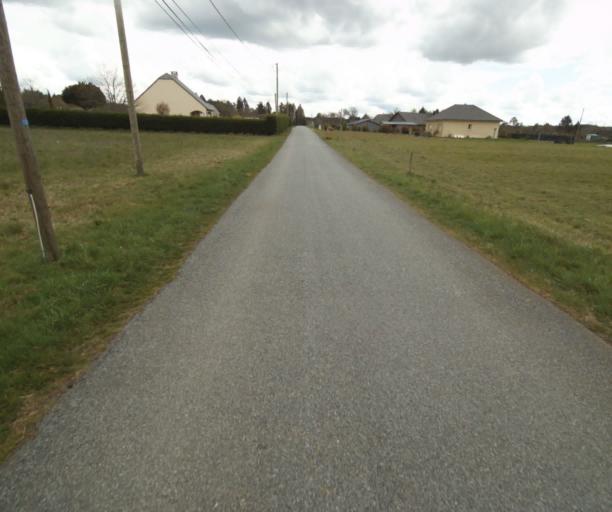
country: FR
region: Limousin
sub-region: Departement de la Correze
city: Correze
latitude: 45.3194
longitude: 1.9220
